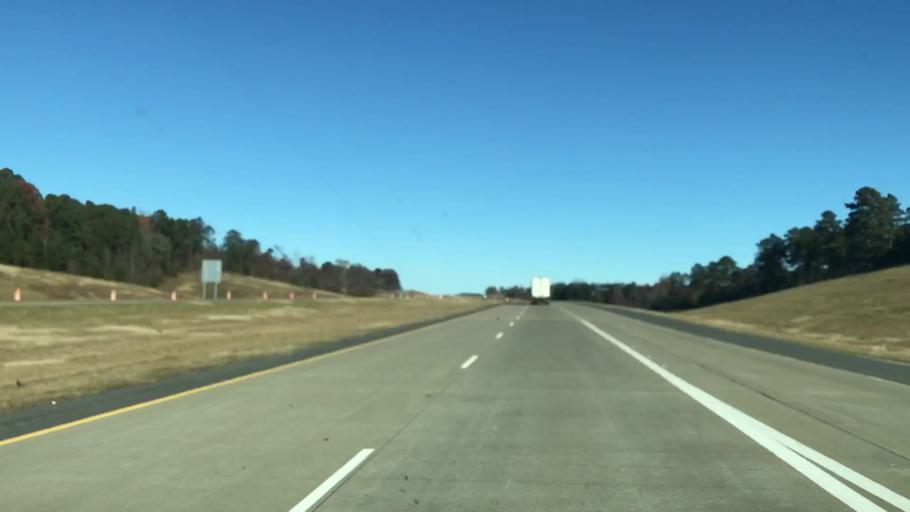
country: US
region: Louisiana
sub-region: Caddo Parish
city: Vivian
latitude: 32.9468
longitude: -93.8982
